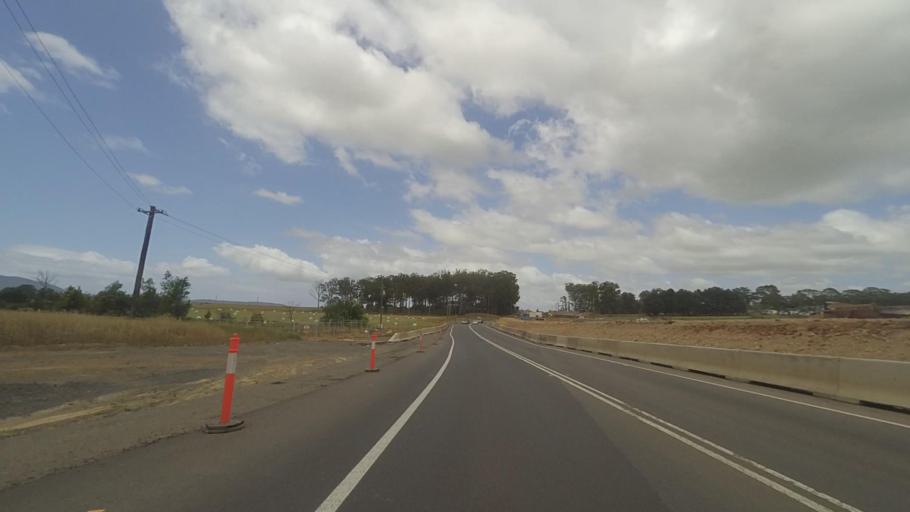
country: AU
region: New South Wales
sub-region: Shoalhaven Shire
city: Berry
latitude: -34.7794
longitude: 150.6813
